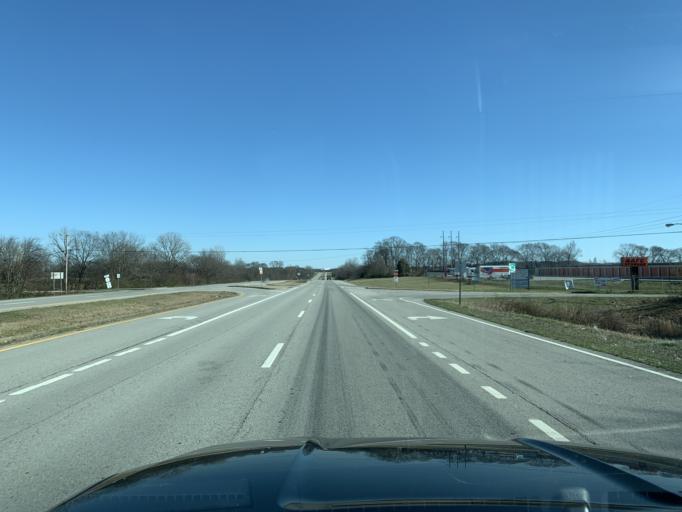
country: US
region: Tennessee
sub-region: Maury County
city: Mount Pleasant
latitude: 35.5512
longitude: -87.2097
